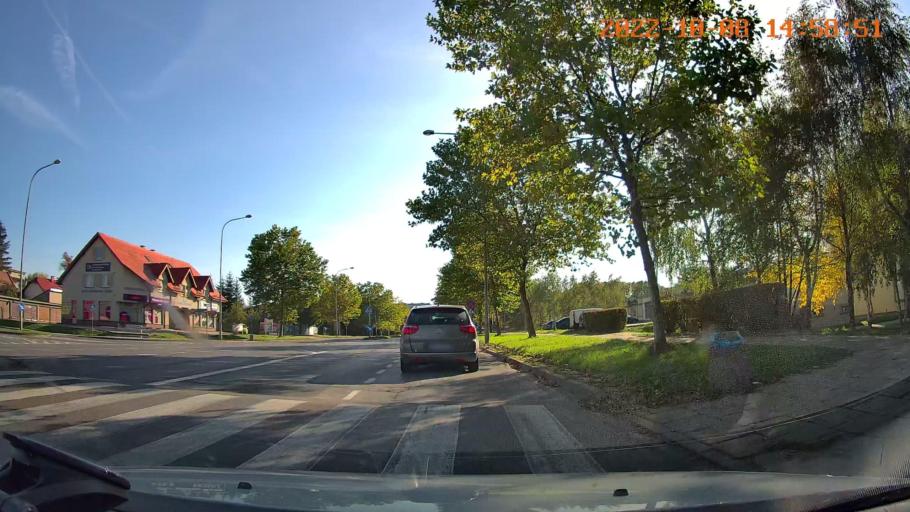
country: PL
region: Lesser Poland Voivodeship
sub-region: Powiat tarnowski
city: Tarnow
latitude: 50.0218
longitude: 20.9972
